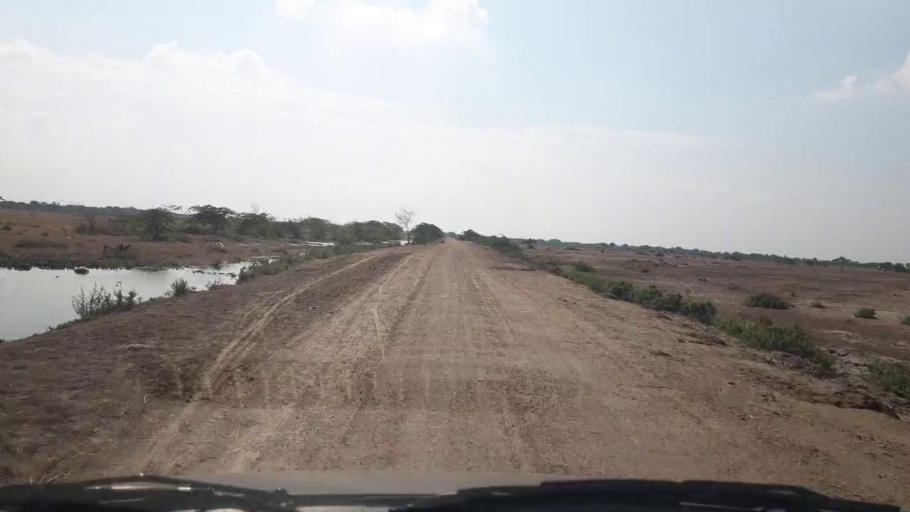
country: PK
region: Sindh
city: Badin
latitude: 24.4948
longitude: 68.6119
